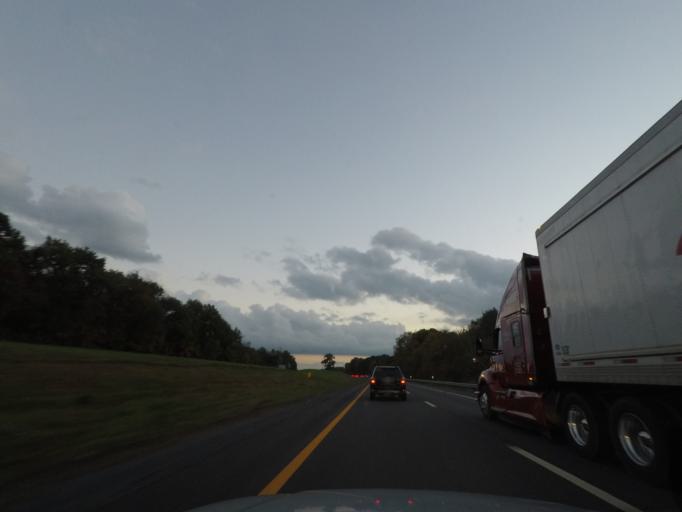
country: US
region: New York
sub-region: Ulster County
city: New Paltz
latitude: 41.7237
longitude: -74.0701
